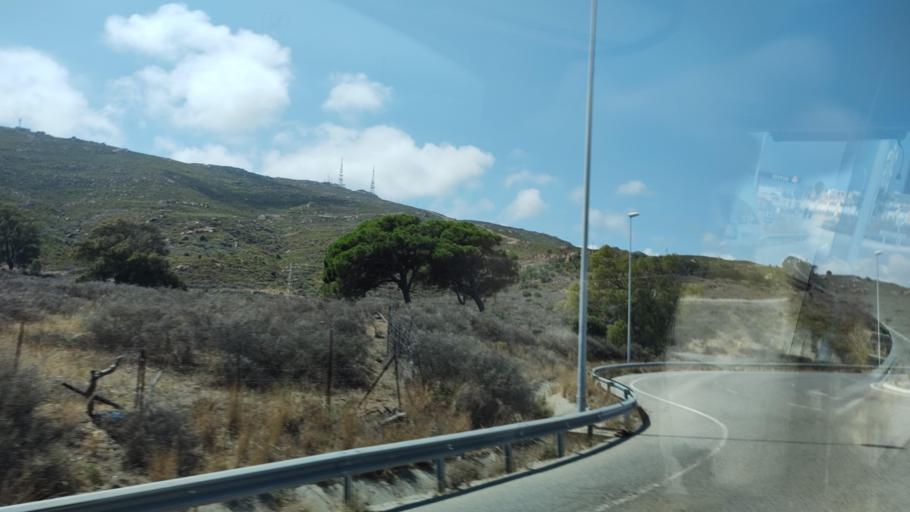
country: ES
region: Andalusia
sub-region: Provincia de Cadiz
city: La Linea de la Concepcion
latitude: 36.1983
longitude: -5.3468
